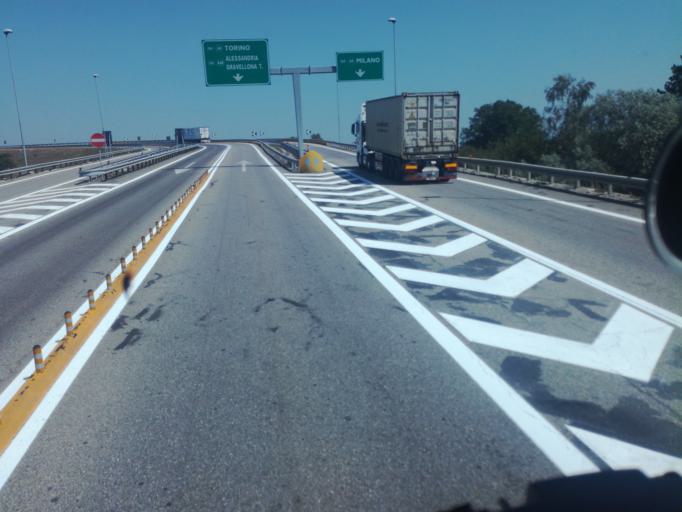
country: IT
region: Piedmont
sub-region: Provincia di Novara
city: Pernate
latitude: 45.4669
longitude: 8.6772
